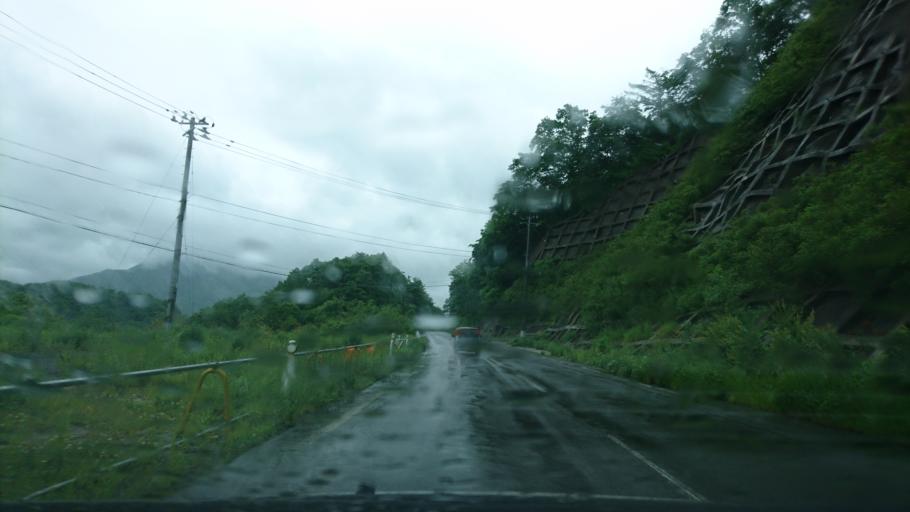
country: JP
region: Iwate
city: Ichinoseki
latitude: 39.0071
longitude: 140.8946
